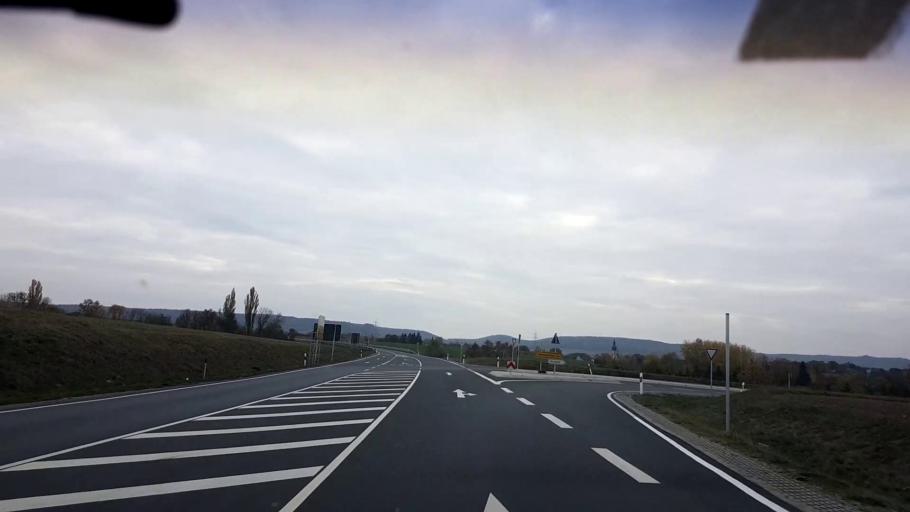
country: DE
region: Bavaria
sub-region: Regierungsbezirk Unterfranken
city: Wiesentheid
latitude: 49.7726
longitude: 10.3458
